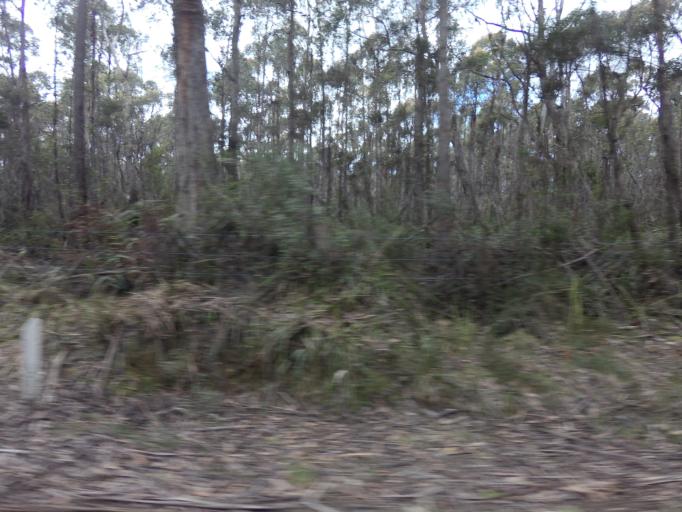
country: AU
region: Tasmania
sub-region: Huon Valley
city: Geeveston
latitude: -43.4250
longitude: 147.0061
